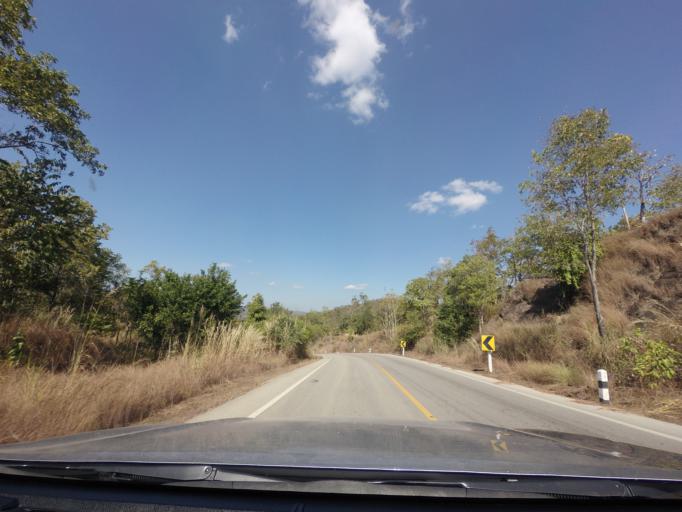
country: TH
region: Lampang
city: Chae Hom
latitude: 18.5742
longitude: 99.6270
